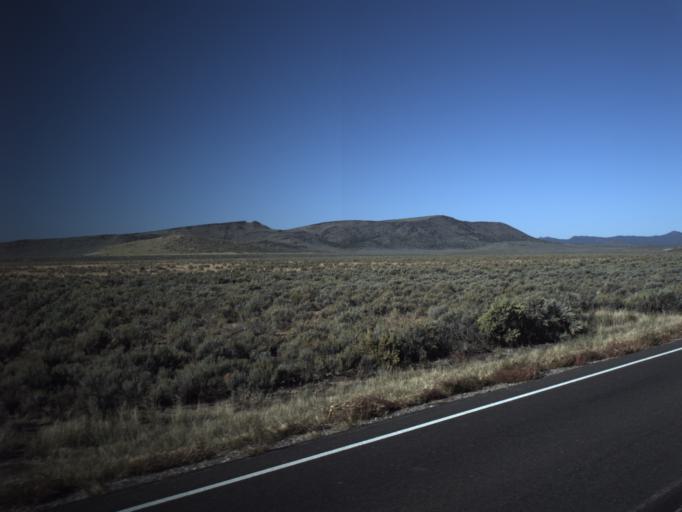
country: US
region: Utah
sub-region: Washington County
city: Enterprise
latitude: 37.7736
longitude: -113.8382
